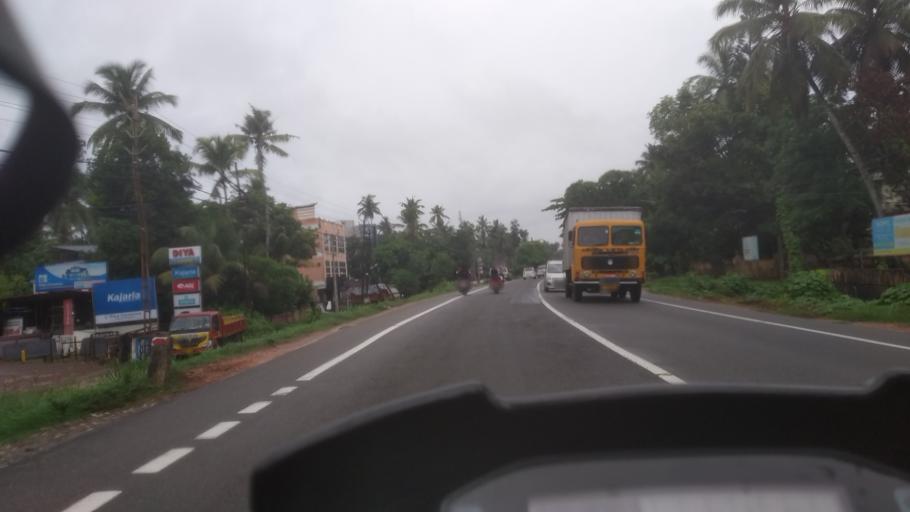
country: IN
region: Kerala
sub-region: Alappuzha
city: Kayankulam
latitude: 9.1632
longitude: 76.5039
